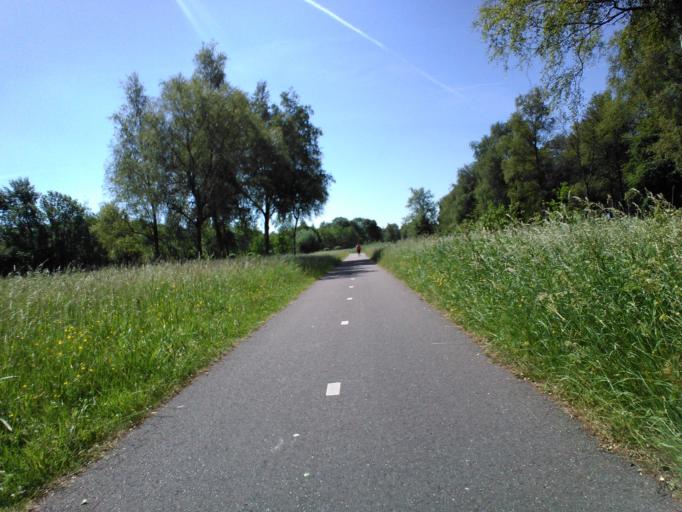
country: NL
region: South Holland
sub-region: Molenwaard
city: Nieuw-Lekkerland
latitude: 51.9299
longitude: 4.6939
